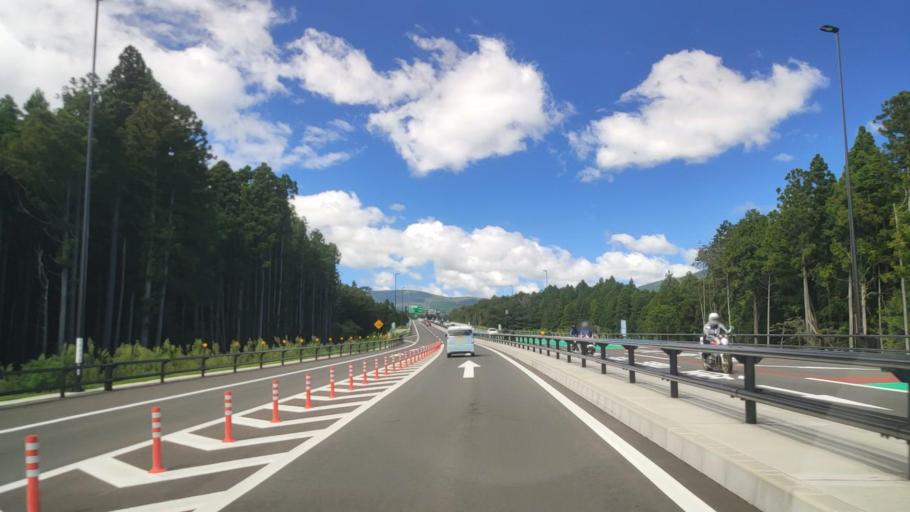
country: JP
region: Shizuoka
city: Gotemba
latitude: 35.3296
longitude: 138.9001
